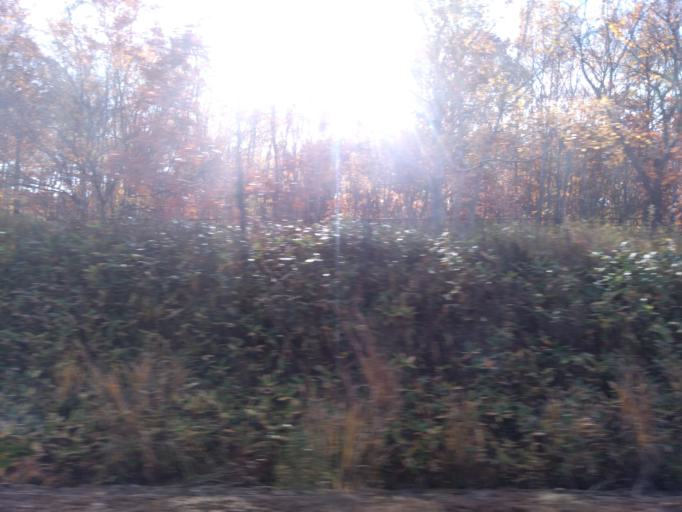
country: JP
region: Hokkaido
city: Kitahiroshima
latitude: 42.9995
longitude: 141.5267
